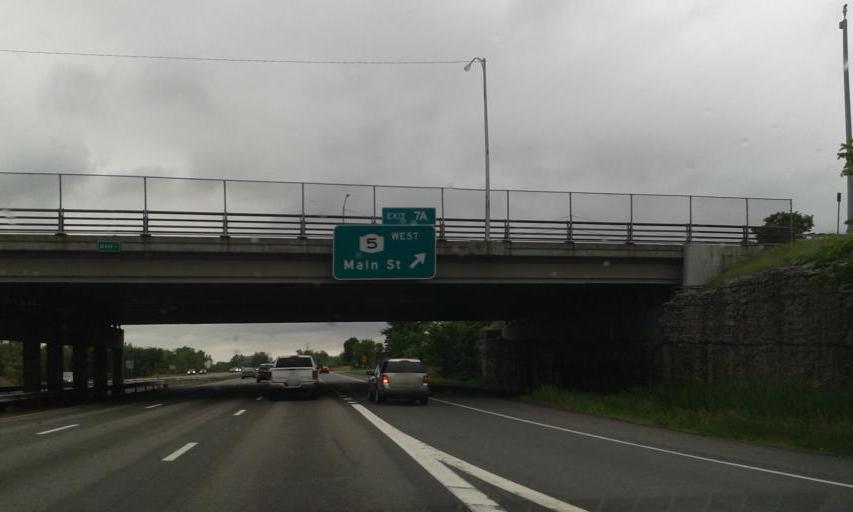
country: US
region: New York
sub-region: Erie County
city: Williamsville
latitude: 42.9580
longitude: -78.7662
